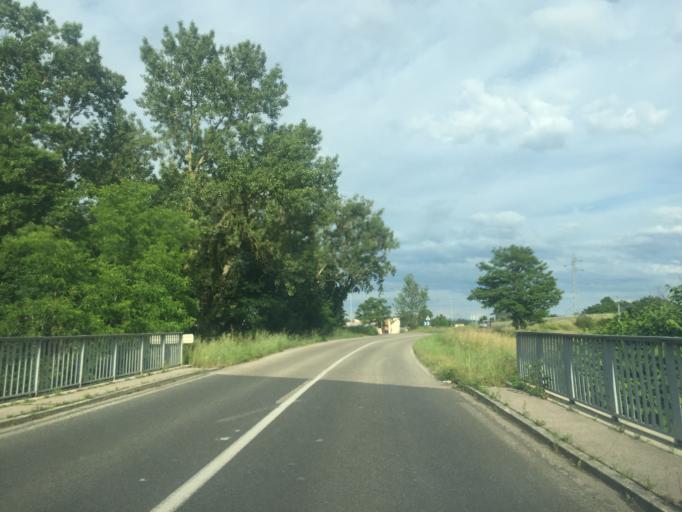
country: FR
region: Rhone-Alpes
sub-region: Departement de l'Ain
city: Beynost
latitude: 45.8280
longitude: 5.0106
